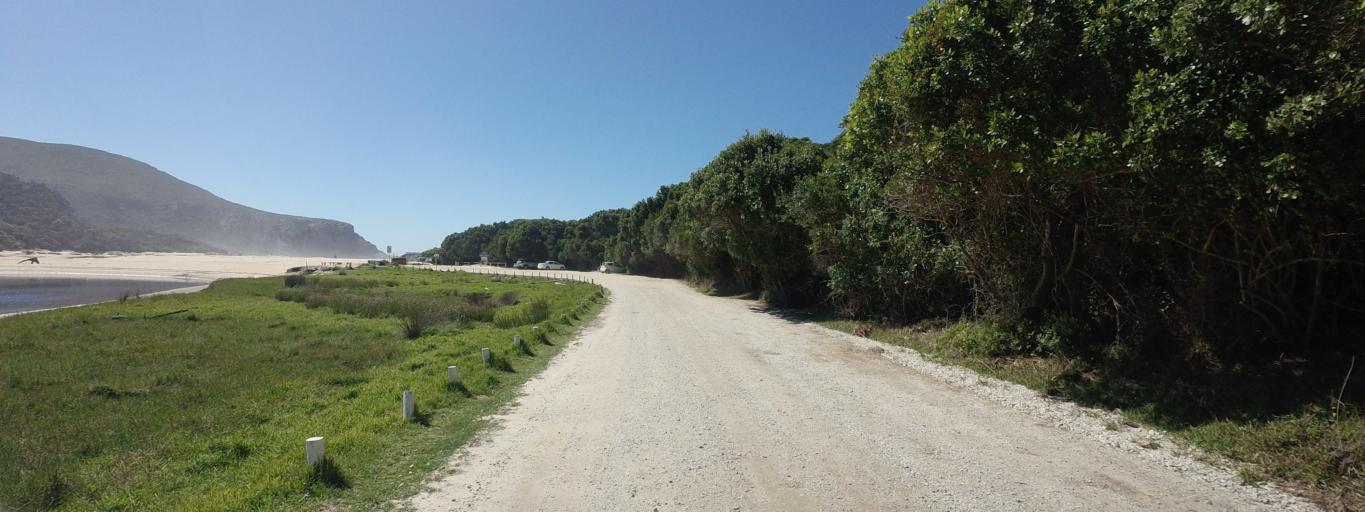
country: ZA
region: Western Cape
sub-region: Eden District Municipality
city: Plettenberg Bay
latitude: -33.9803
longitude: 23.5656
